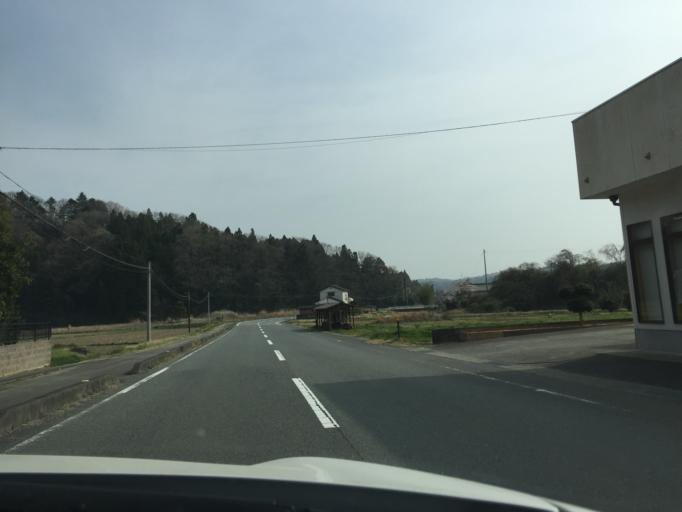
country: JP
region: Fukushima
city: Iwaki
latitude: 36.9822
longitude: 140.8012
